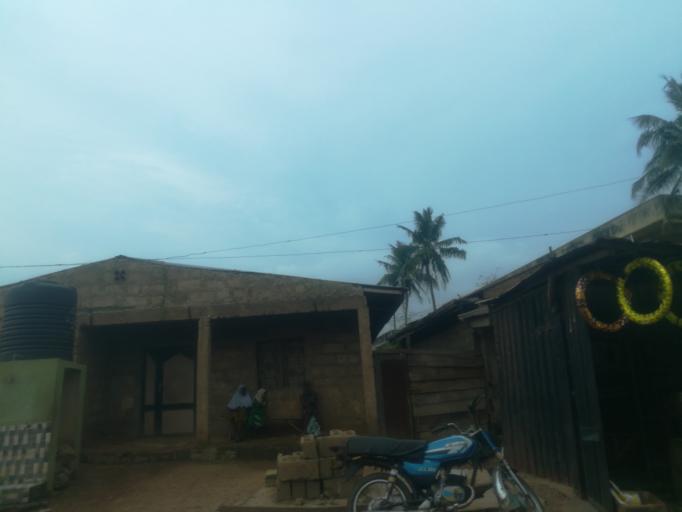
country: NG
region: Oyo
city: Ibadan
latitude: 7.4365
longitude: 3.9210
